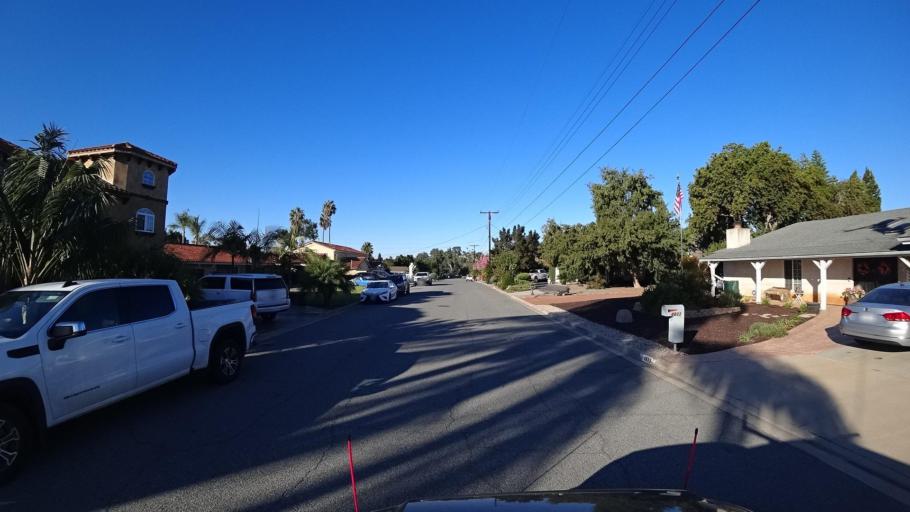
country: US
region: California
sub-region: San Diego County
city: Bonita
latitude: 32.6735
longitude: -117.0278
